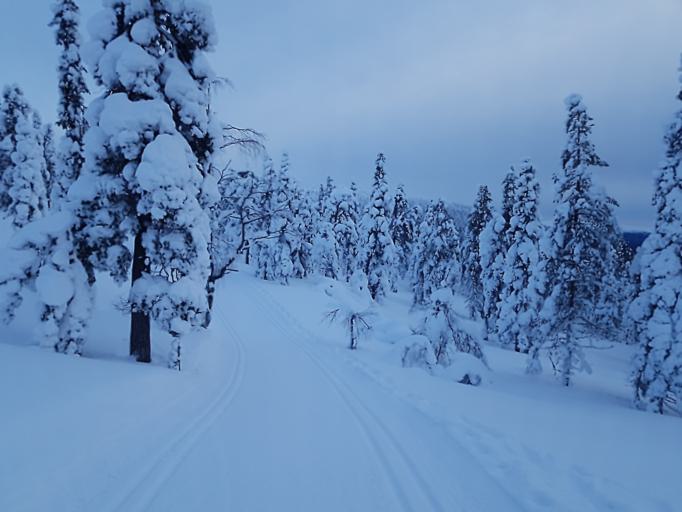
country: FI
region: Lapland
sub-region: Tunturi-Lappi
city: Kolari
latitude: 67.6564
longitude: 24.2423
